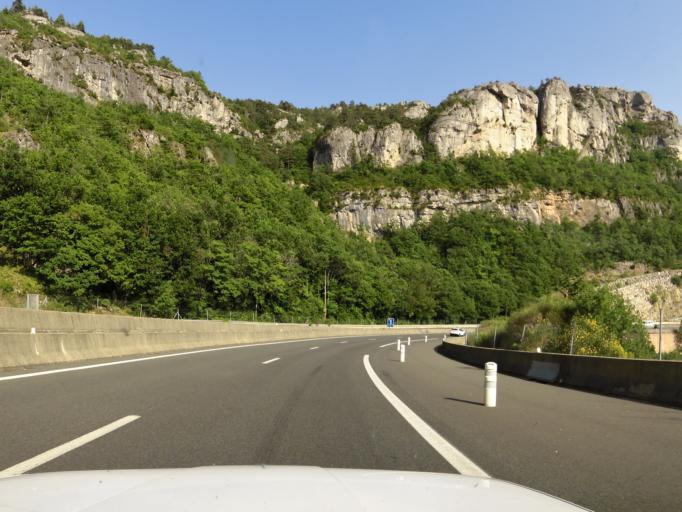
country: FR
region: Languedoc-Roussillon
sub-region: Departement de l'Herault
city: Lodeve
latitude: 43.8238
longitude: 3.3196
